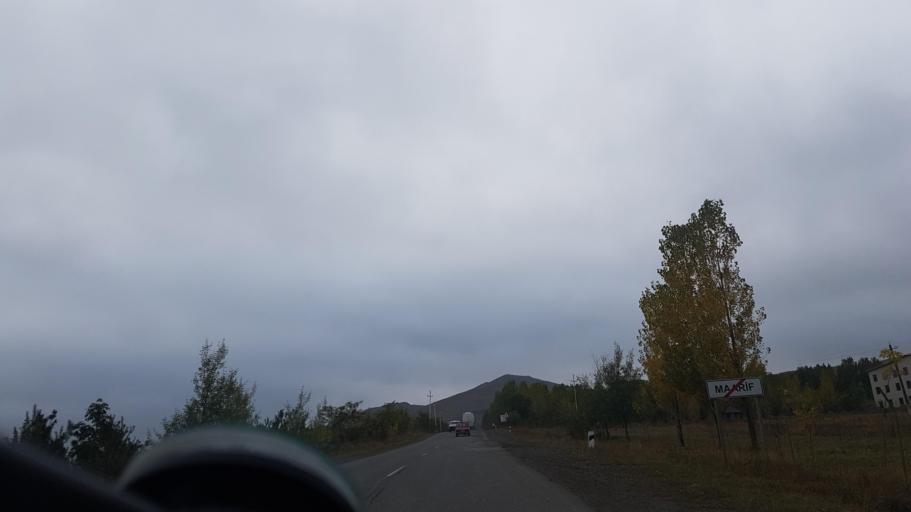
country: AZ
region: Gadabay Rayon
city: Ariqdam
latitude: 40.6317
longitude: 45.8138
